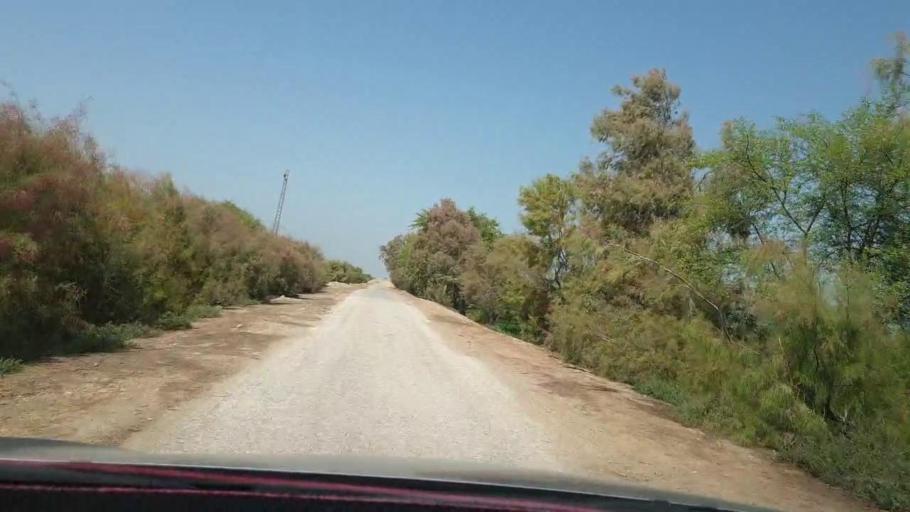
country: PK
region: Sindh
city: Warah
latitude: 27.5590
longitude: 67.7405
